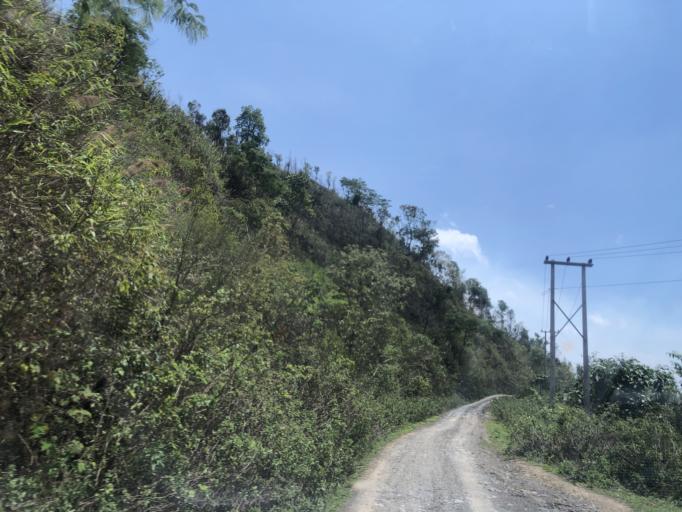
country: LA
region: Phongsali
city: Phongsali
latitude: 21.4380
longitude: 102.1622
